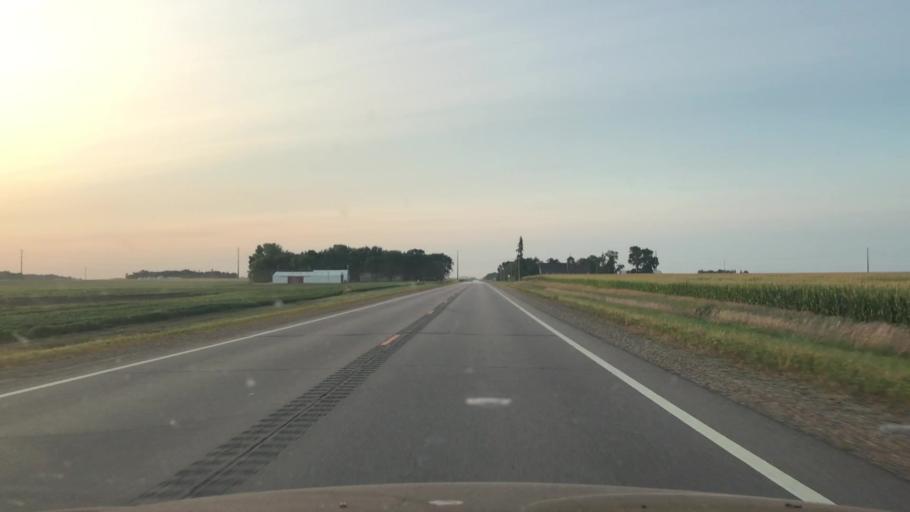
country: US
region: Minnesota
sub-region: Redwood County
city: Redwood Falls
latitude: 44.4237
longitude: -95.1175
